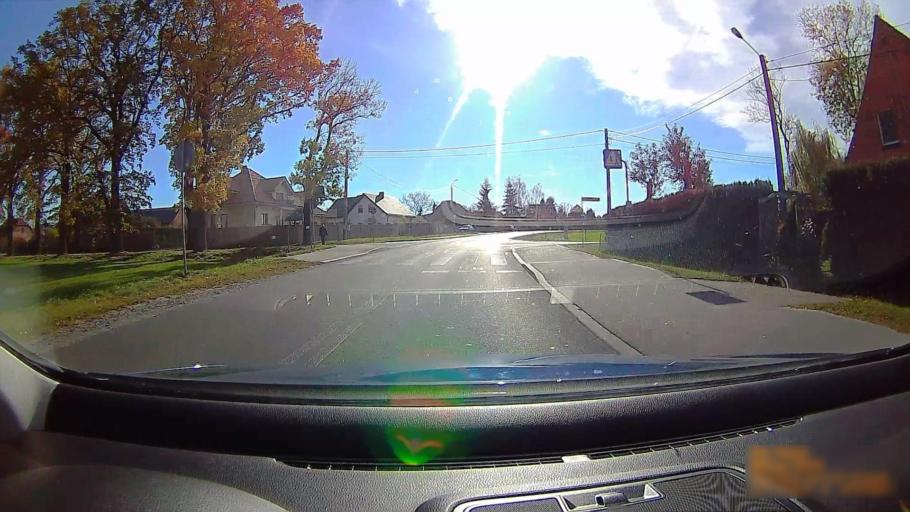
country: PL
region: Greater Poland Voivodeship
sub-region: Powiat ostrzeszowski
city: Doruchow
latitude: 51.3595
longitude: 18.0304
